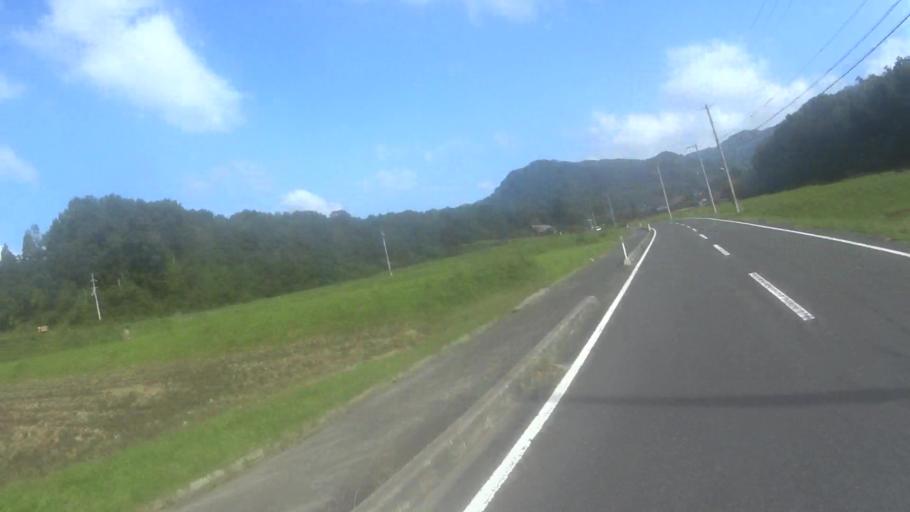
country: JP
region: Kyoto
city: Miyazu
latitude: 35.6037
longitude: 135.1467
